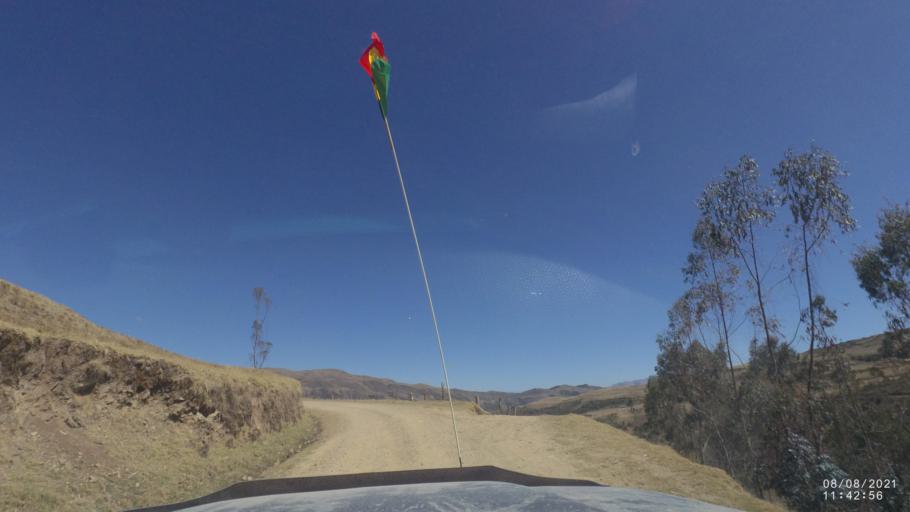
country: BO
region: Cochabamba
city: Colchani
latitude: -16.7985
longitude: -66.6402
